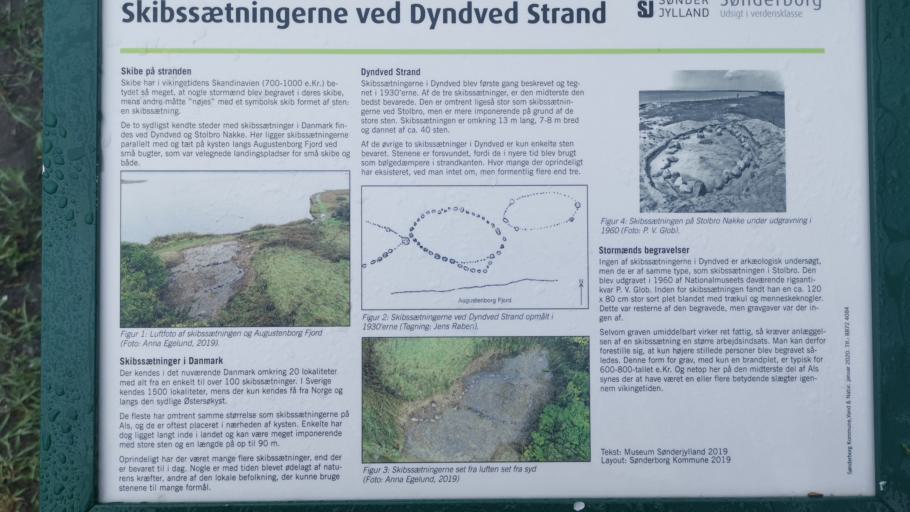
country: DK
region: South Denmark
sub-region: Sonderborg Kommune
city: Guderup
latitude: 54.9746
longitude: 9.8349
